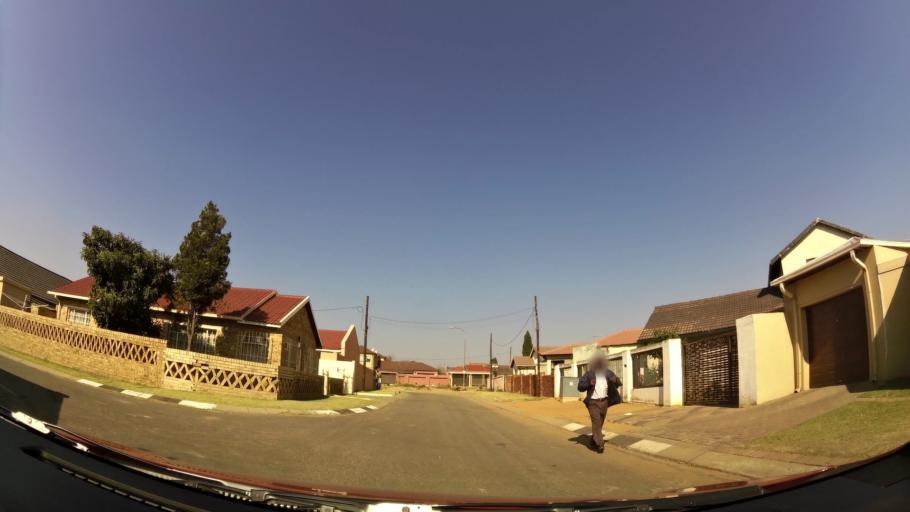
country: ZA
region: Gauteng
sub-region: City of Johannesburg Metropolitan Municipality
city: Johannesburg
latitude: -26.2460
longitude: 27.9596
